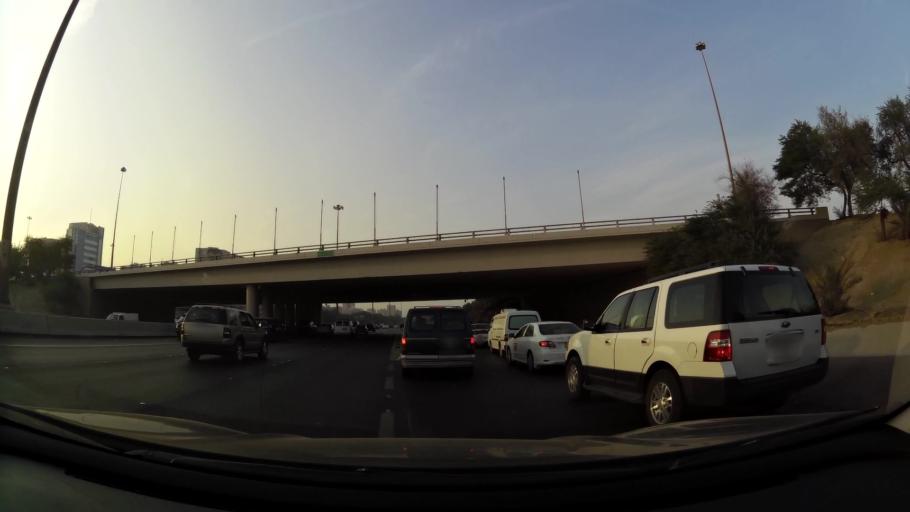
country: KW
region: Muhafazat Hawalli
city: Hawalli
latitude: 29.3305
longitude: 48.0402
